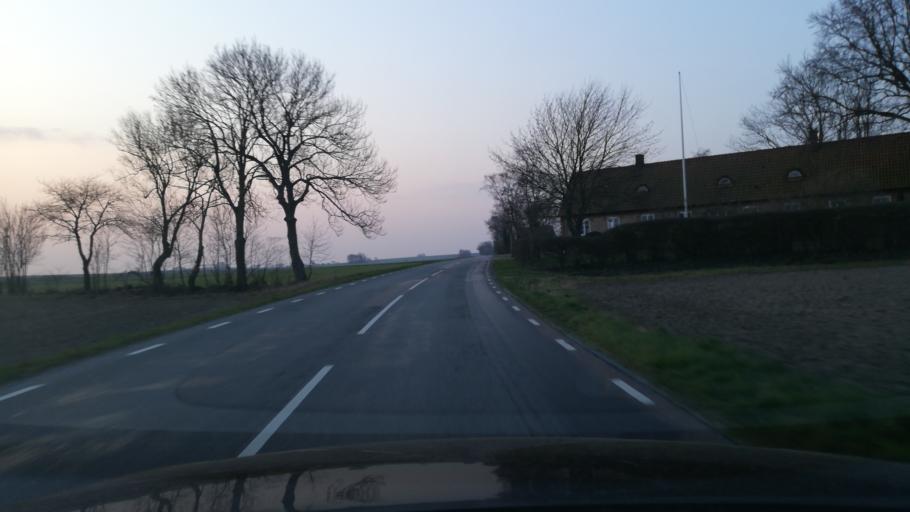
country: SE
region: Skane
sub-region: Ystads Kommun
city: Kopingebro
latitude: 55.4589
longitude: 14.1080
